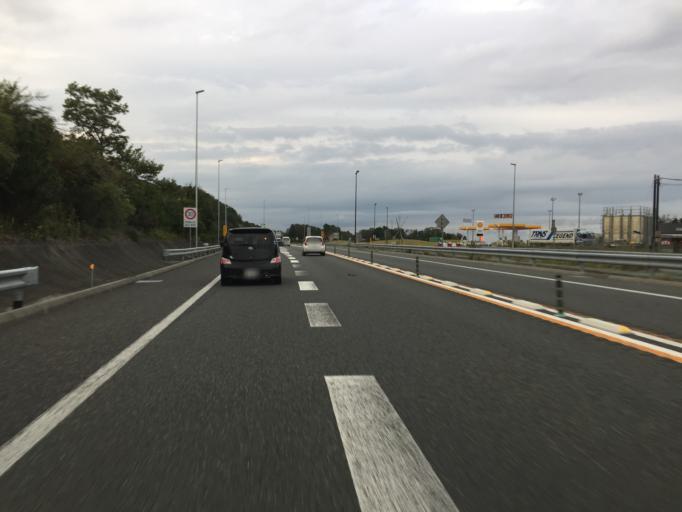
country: JP
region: Fukushima
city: Namie
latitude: 37.7126
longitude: 140.9213
